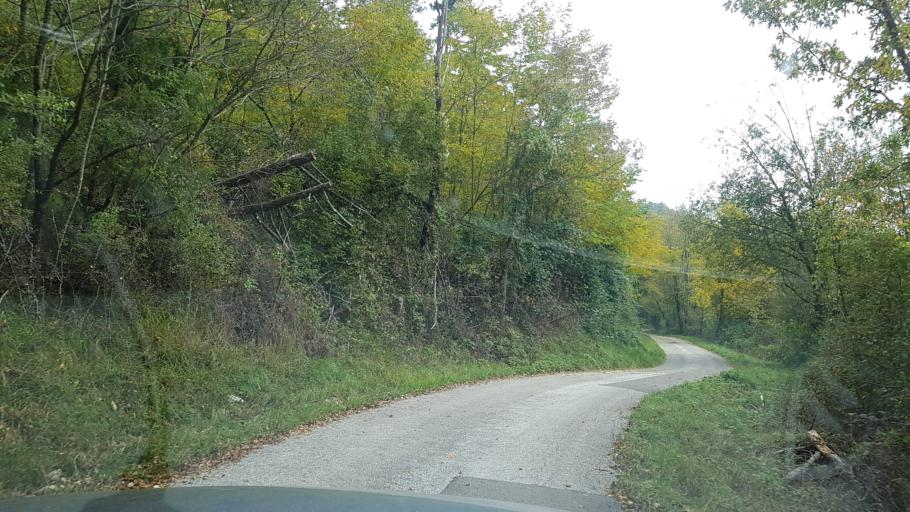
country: HR
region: Istarska
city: Buzet
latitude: 45.4337
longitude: 14.0621
